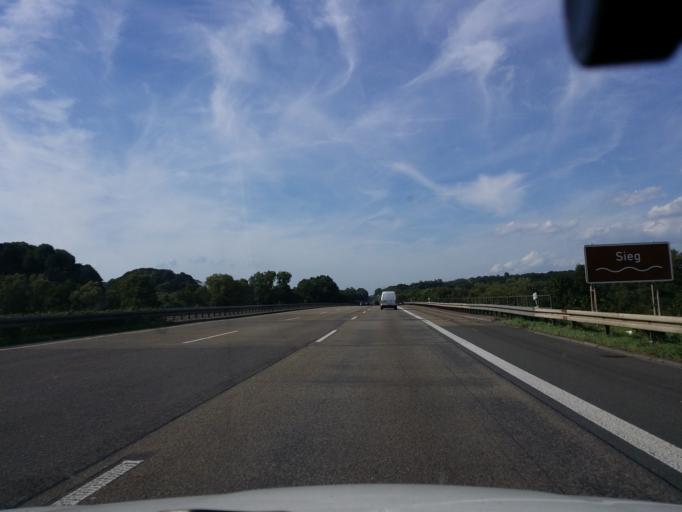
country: DE
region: North Rhine-Westphalia
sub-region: Regierungsbezirk Koln
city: Stossdorf
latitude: 50.7915
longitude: 7.2351
